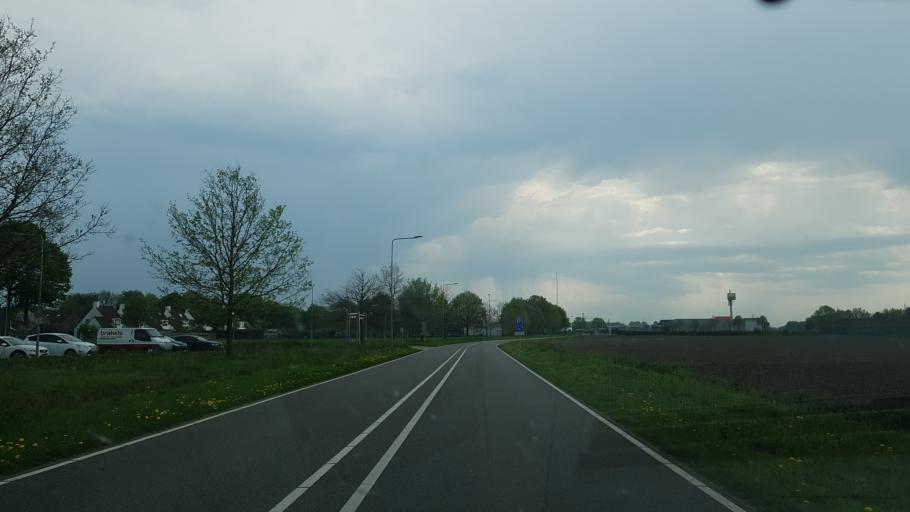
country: NL
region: Limburg
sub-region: Gemeente Nederweert
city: Nederweert
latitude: 51.2815
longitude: 5.7360
